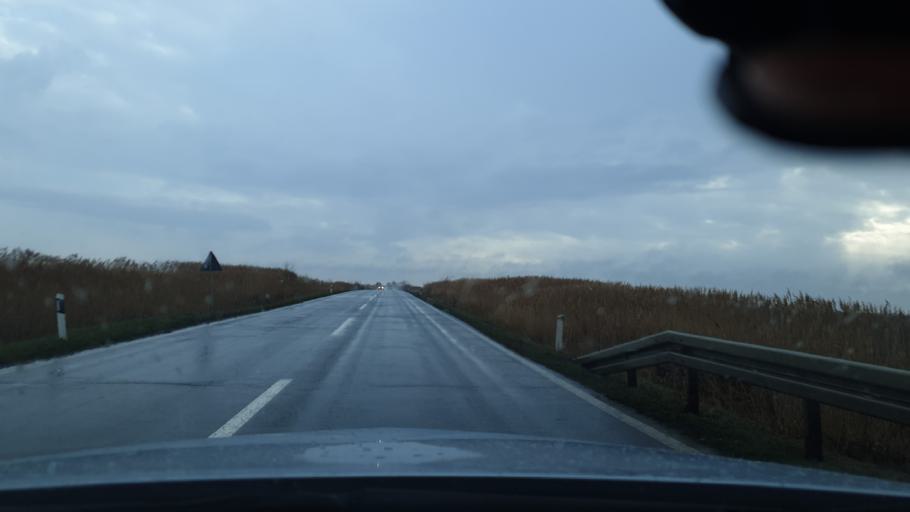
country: RS
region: Autonomna Pokrajina Vojvodina
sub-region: Juznobanatski Okrug
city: Pancevo
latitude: 44.8377
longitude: 20.8082
